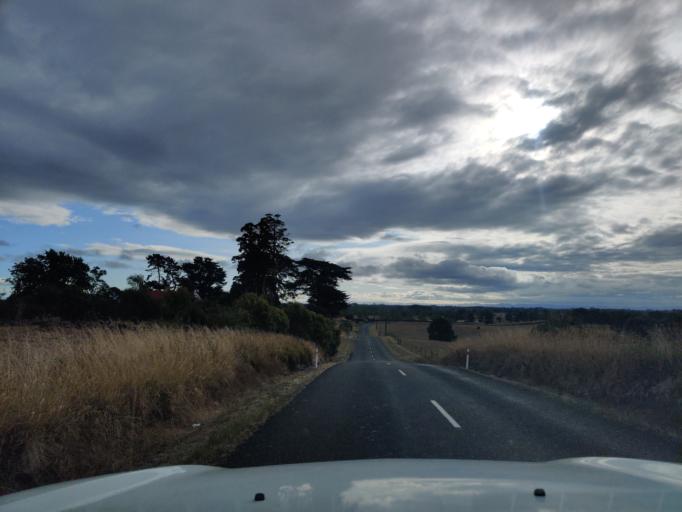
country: NZ
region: Waikato
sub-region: Waipa District
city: Cambridge
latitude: -37.7959
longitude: 175.4447
